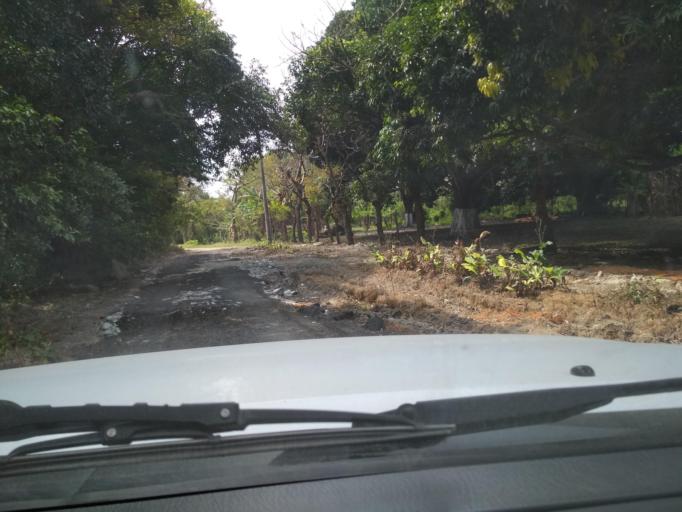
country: MX
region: Veracruz
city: El Tejar
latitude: 19.0754
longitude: -96.1711
